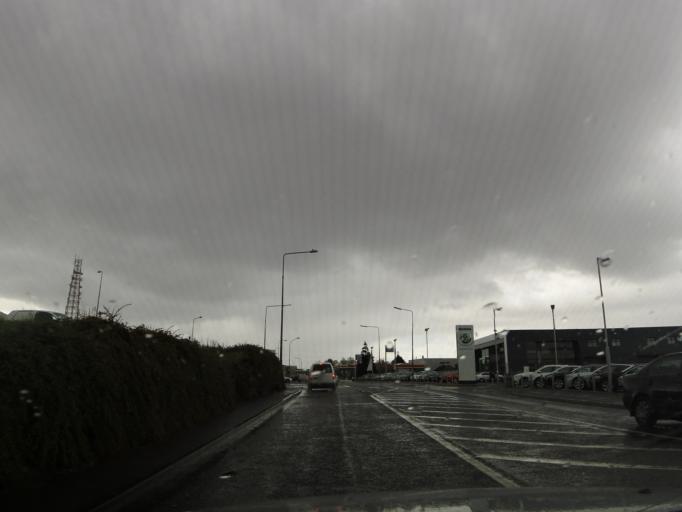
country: IE
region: Connaught
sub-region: County Galway
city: Gaillimh
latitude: 53.2934
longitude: -9.0175
